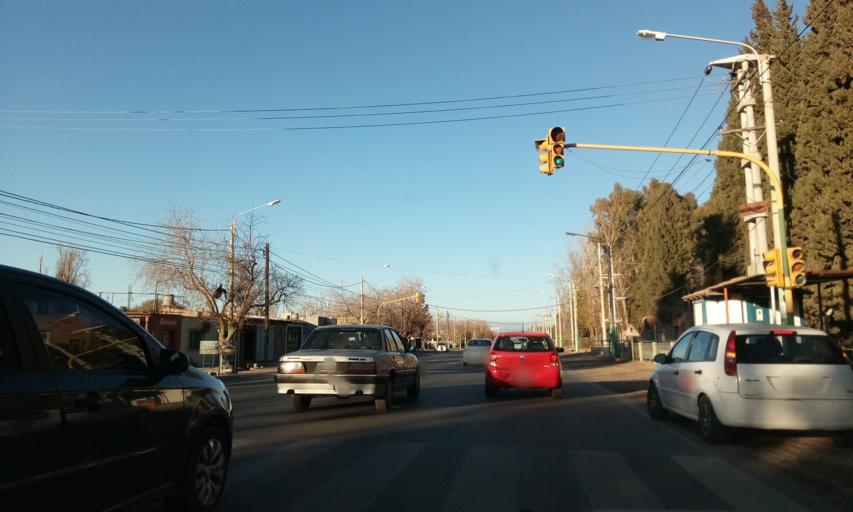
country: AR
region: San Juan
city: San Juan
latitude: -31.5388
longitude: -68.5871
